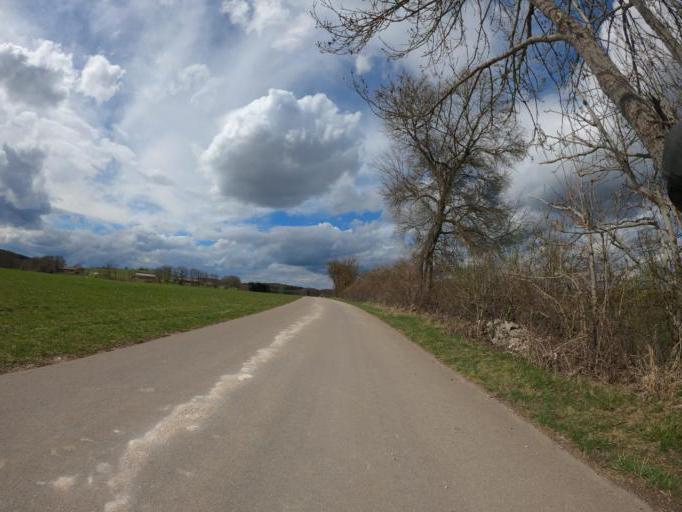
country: DE
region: Baden-Wuerttemberg
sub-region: Tuebingen Region
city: Pfullingen
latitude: 48.3965
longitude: 9.1743
